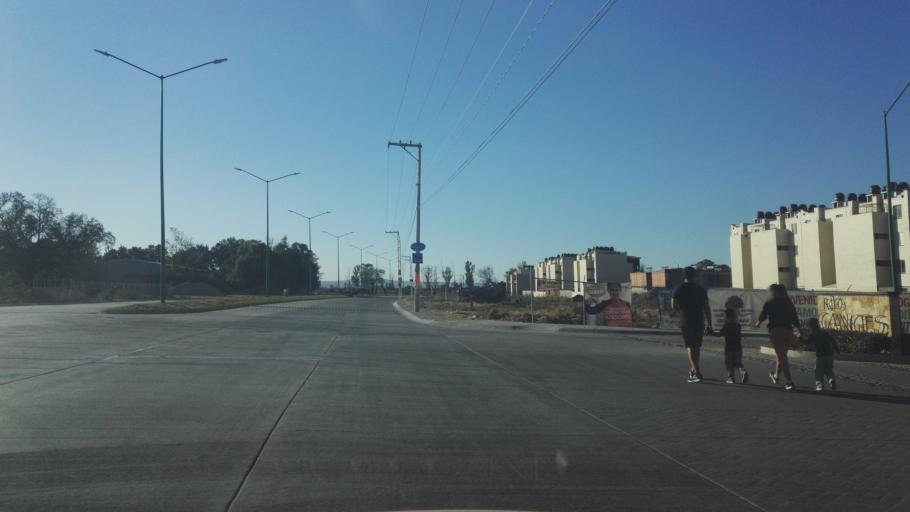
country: MX
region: Guanajuato
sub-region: Leon
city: Fraccionamiento Paraiso Real
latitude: 21.0644
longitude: -101.6088
